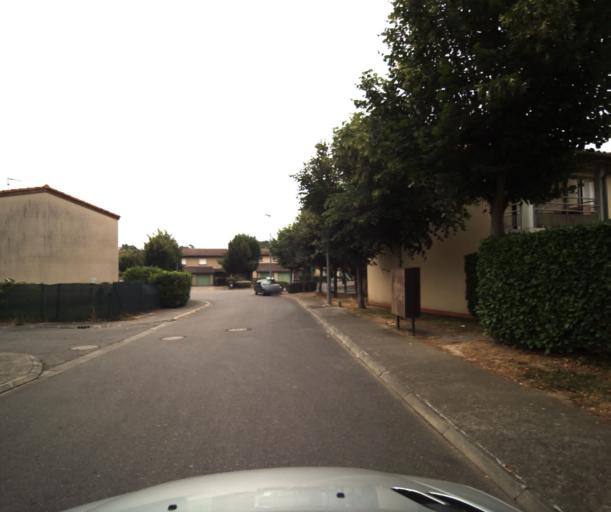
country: FR
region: Midi-Pyrenees
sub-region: Departement de la Haute-Garonne
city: Portet-sur-Garonne
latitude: 43.5302
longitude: 1.4141
